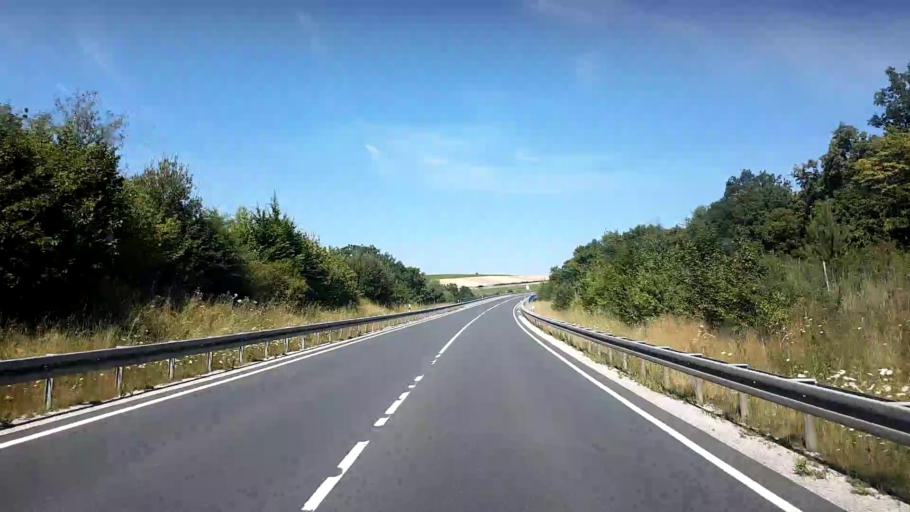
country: DE
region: Bavaria
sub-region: Upper Franconia
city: Untersiemau
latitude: 50.1655
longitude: 11.0016
